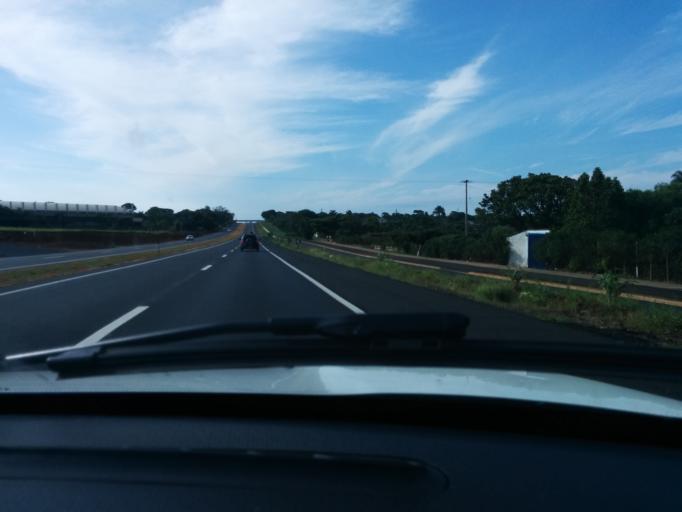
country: BR
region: Sao Paulo
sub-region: Franca
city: Franca
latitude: -20.4496
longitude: -47.4187
